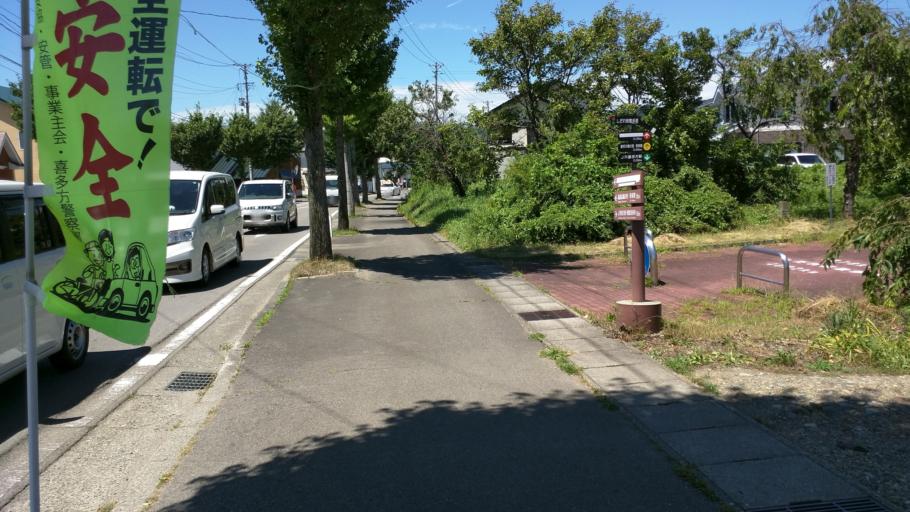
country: JP
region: Fukushima
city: Kitakata
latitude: 37.6465
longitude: 139.8624
